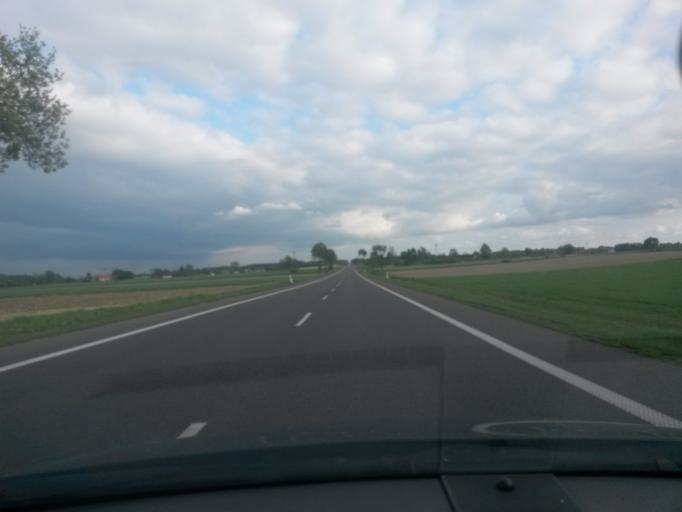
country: PL
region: Masovian Voivodeship
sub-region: Powiat plocki
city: Drobin
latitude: 52.6882
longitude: 20.0529
